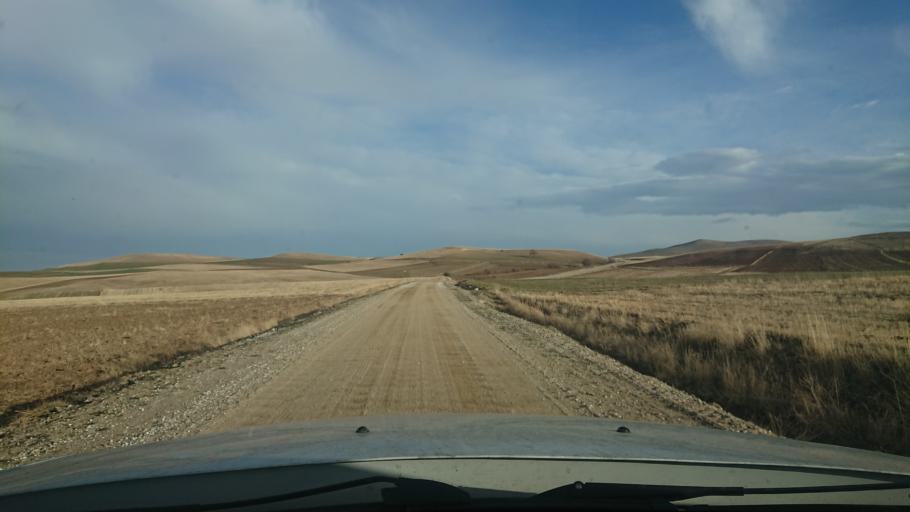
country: TR
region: Aksaray
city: Acipinar
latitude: 38.6919
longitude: 33.8701
